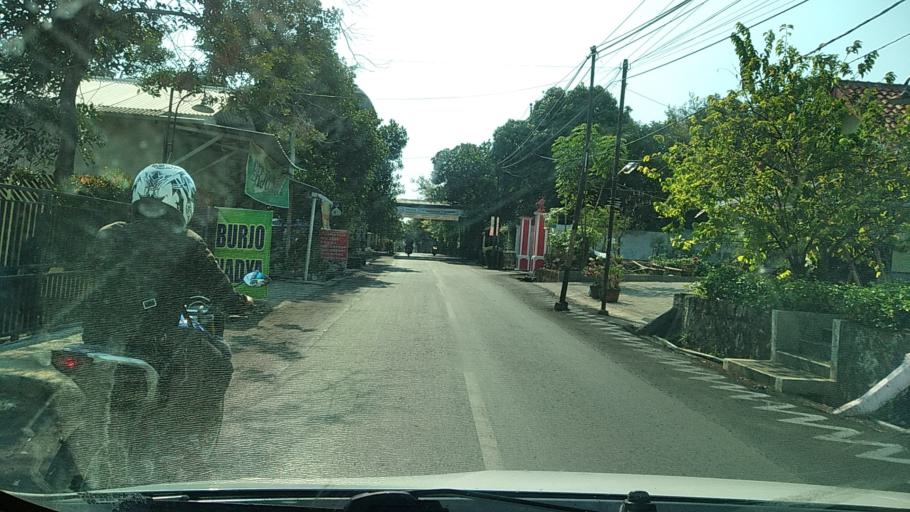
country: ID
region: Central Java
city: Semarang
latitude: -7.0673
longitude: 110.4387
